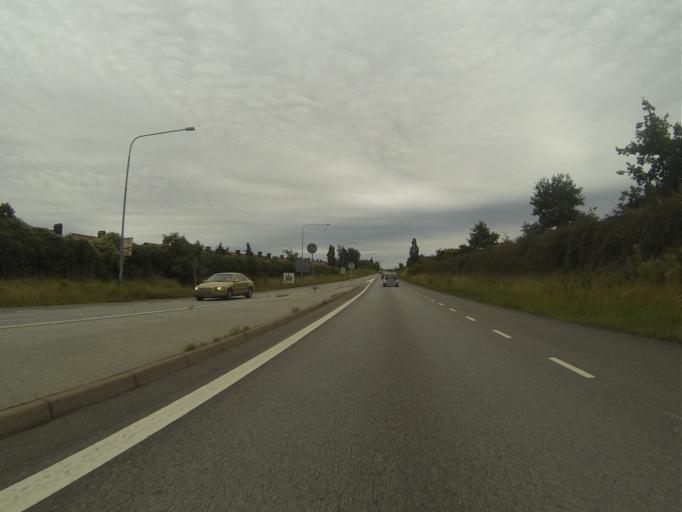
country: SE
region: Skane
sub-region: Burlovs Kommun
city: Arloev
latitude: 55.5945
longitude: 13.0755
